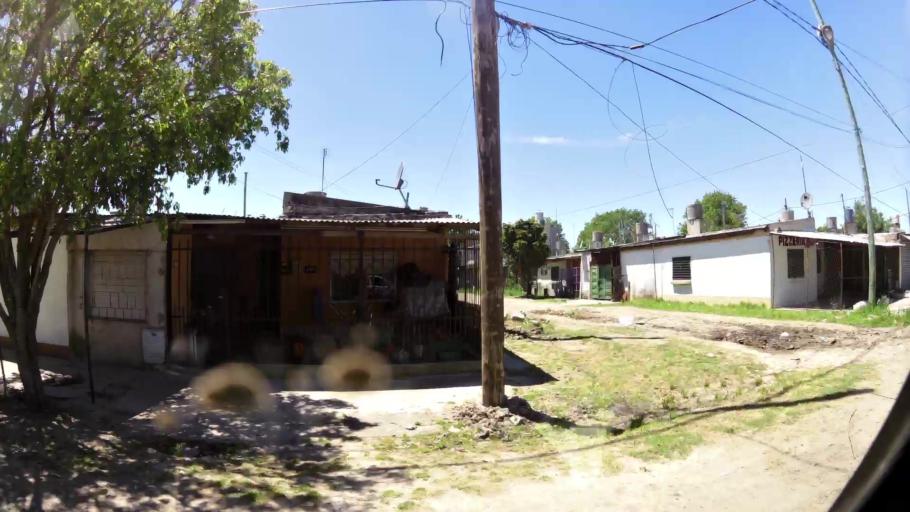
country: AR
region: Buenos Aires
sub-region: Partido de Quilmes
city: Quilmes
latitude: -34.7192
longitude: -58.3207
